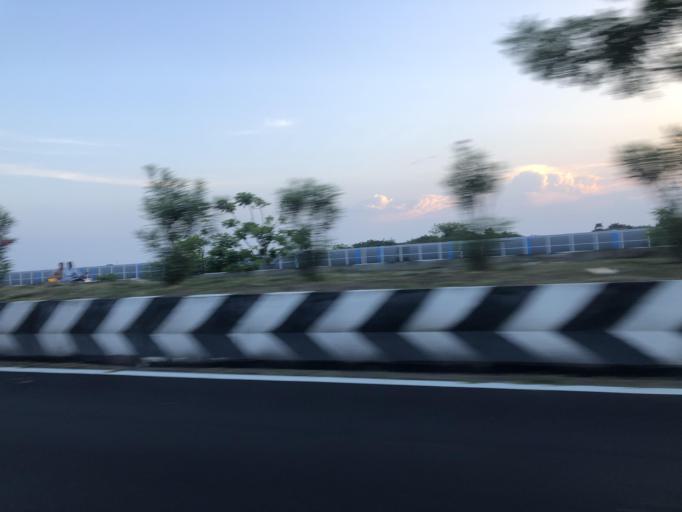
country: IN
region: Tamil Nadu
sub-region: Kancheepuram
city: Injambakkam
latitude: 12.7868
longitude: 80.2441
